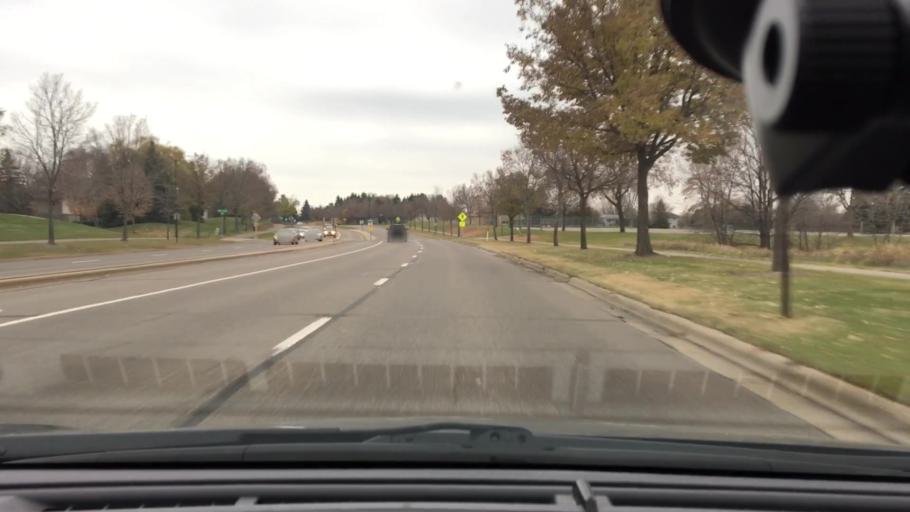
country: US
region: Minnesota
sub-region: Hennepin County
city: Osseo
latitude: 45.1203
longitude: -93.4501
